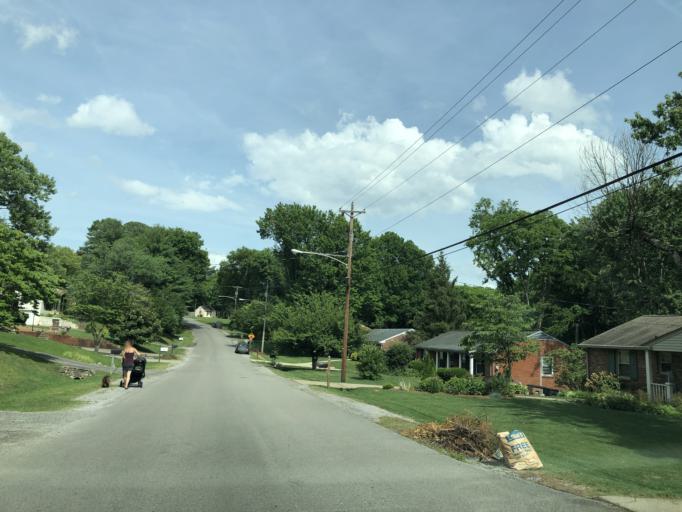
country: US
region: Tennessee
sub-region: Davidson County
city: Oak Hill
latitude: 36.0811
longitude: -86.7418
